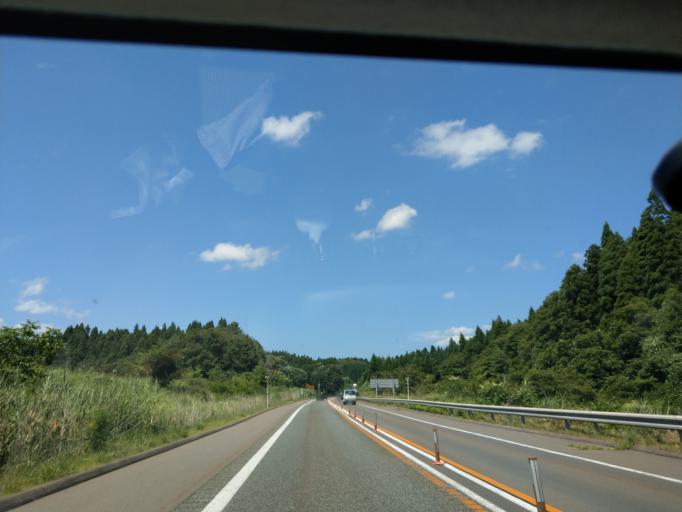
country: JP
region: Akita
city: Akita
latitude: 39.6743
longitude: 140.1868
